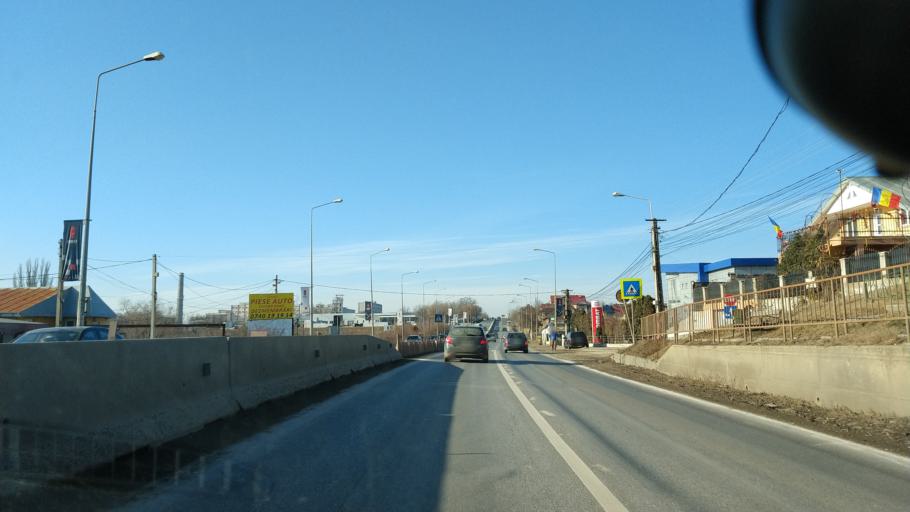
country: RO
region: Iasi
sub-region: Comuna Valea Lupului
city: Valea Lupului
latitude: 47.1751
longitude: 27.4995
